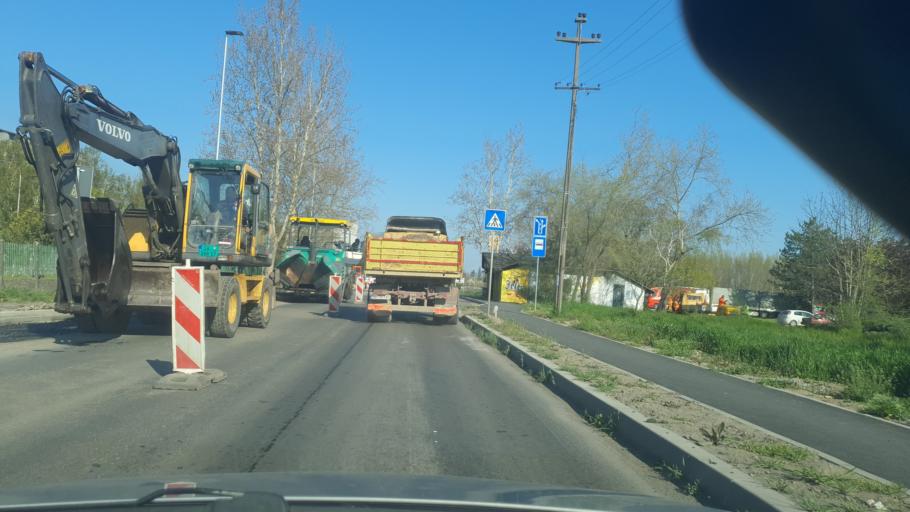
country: RS
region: Autonomna Pokrajina Vojvodina
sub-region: Juznobacki Okrug
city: Vrbas
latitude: 45.5812
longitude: 19.6210
